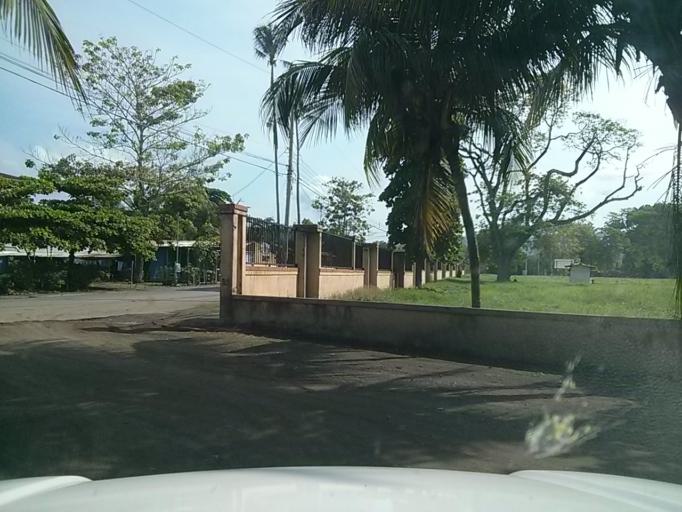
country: CR
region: Puntarenas
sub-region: Canton de Garabito
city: Jaco
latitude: 9.6199
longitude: -84.6377
